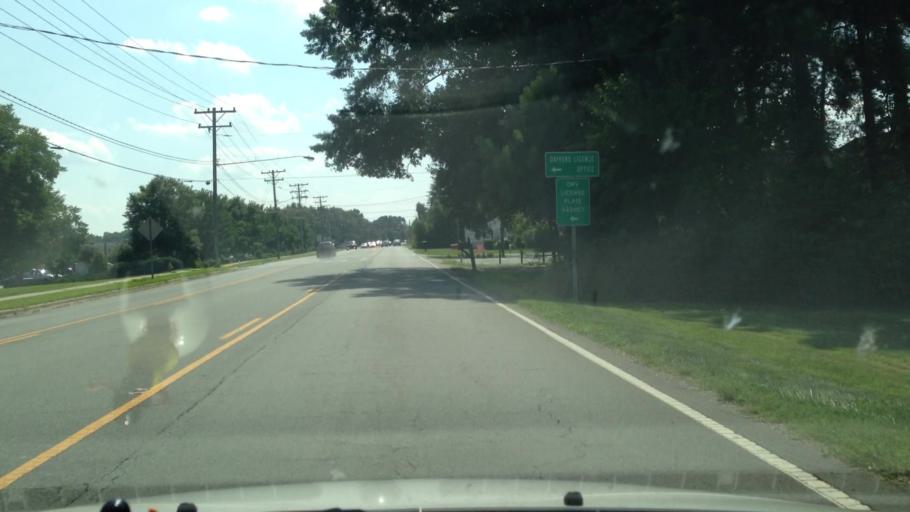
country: US
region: North Carolina
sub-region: Forsyth County
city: Kernersville
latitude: 36.1303
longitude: -80.0579
